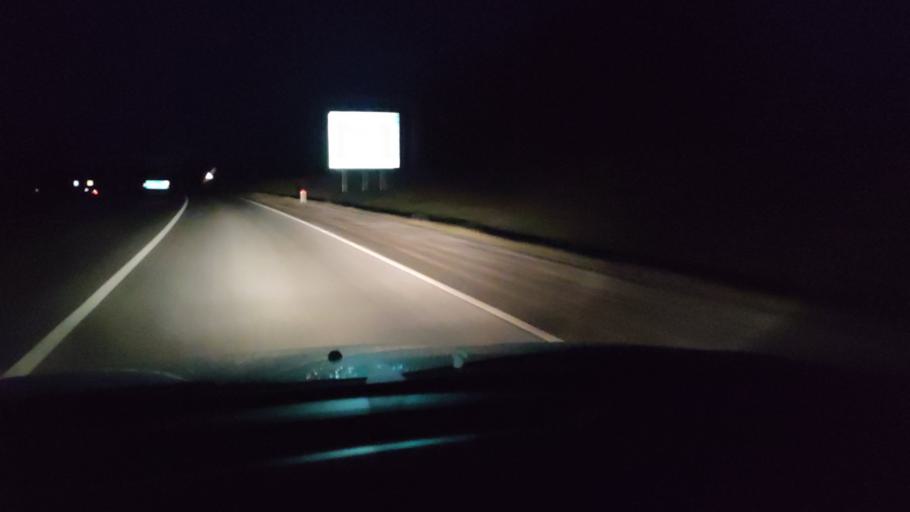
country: RU
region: Perm
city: Siva
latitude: 58.4859
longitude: 54.0681
